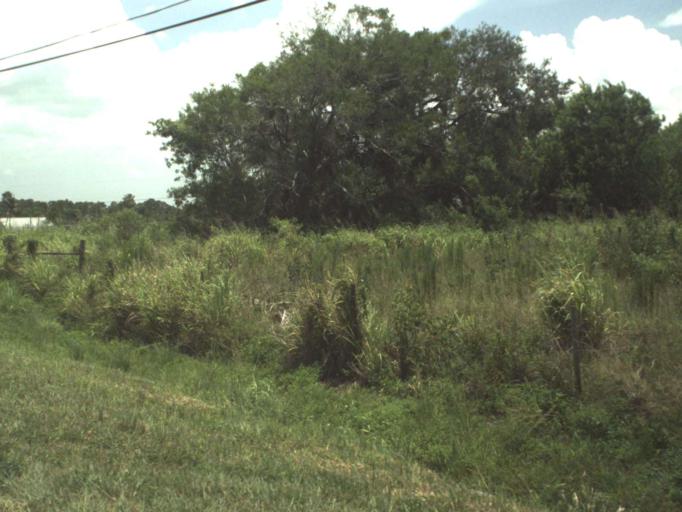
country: US
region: Florida
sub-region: Saint Lucie County
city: Fort Pierce South
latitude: 27.3744
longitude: -80.4407
